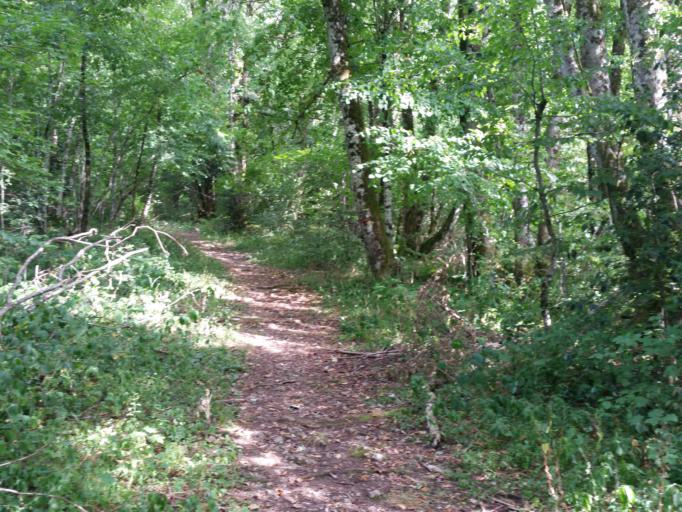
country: FR
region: Franche-Comte
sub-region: Departement du Jura
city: Salins-les-Bains
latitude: 46.9644
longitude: 5.9939
